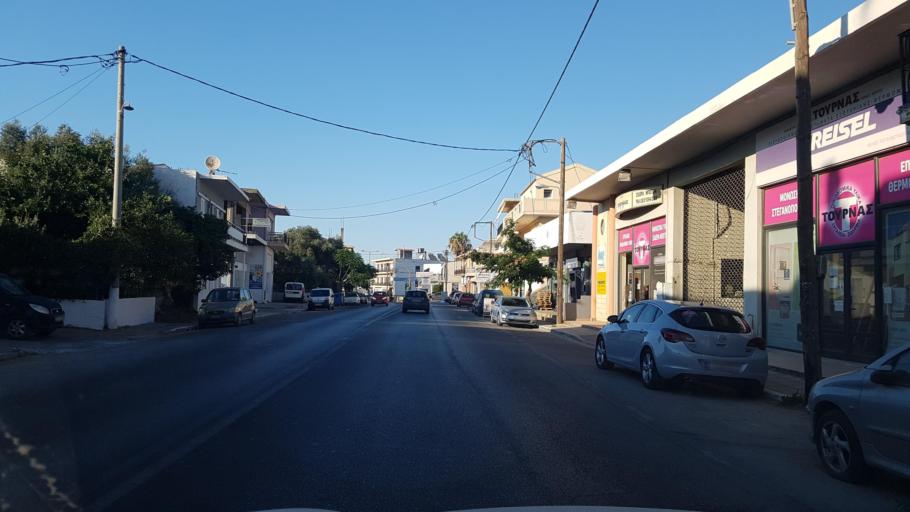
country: GR
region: Crete
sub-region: Nomos Chanias
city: Perivolia
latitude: 35.5041
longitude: 24.0021
